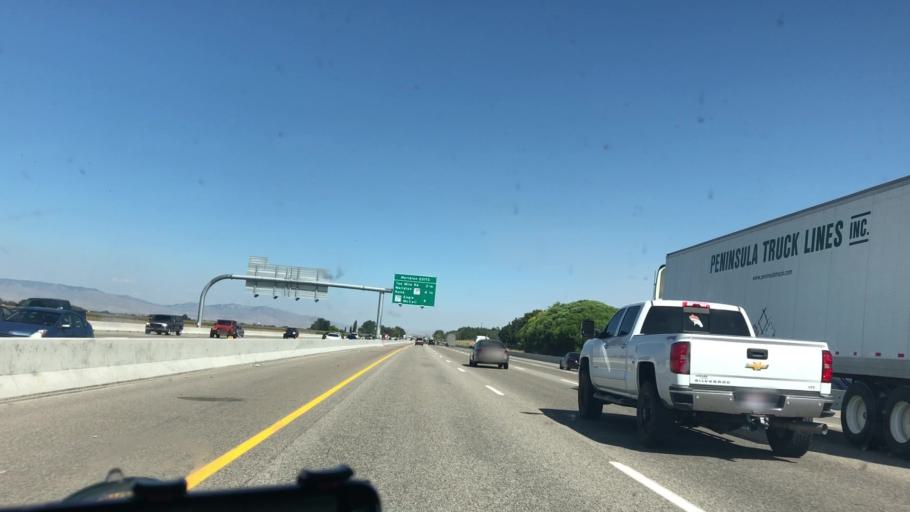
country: US
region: Idaho
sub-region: Ada County
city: Star
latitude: 43.5988
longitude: -116.4889
